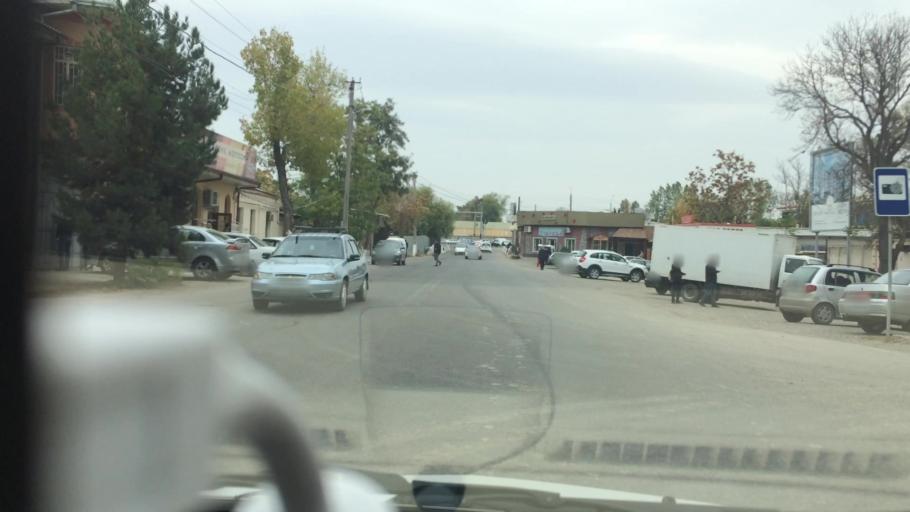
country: UZ
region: Toshkent Shahri
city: Tashkent
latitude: 41.2791
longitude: 69.2707
